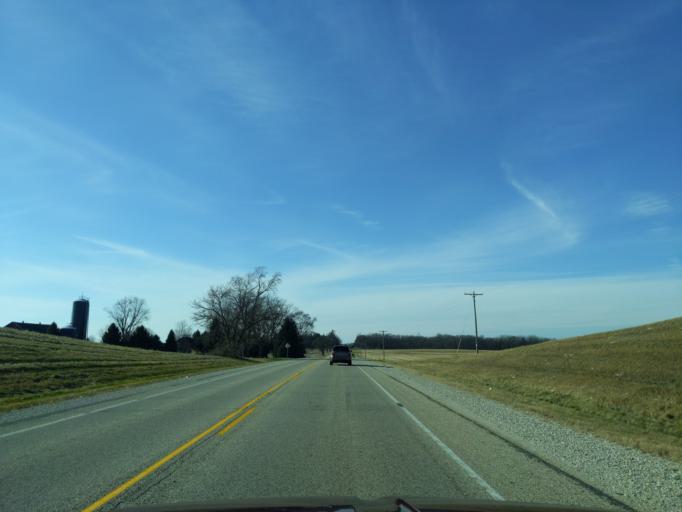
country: US
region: Wisconsin
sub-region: Walworth County
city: Whitewater
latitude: 42.8278
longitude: -88.8036
